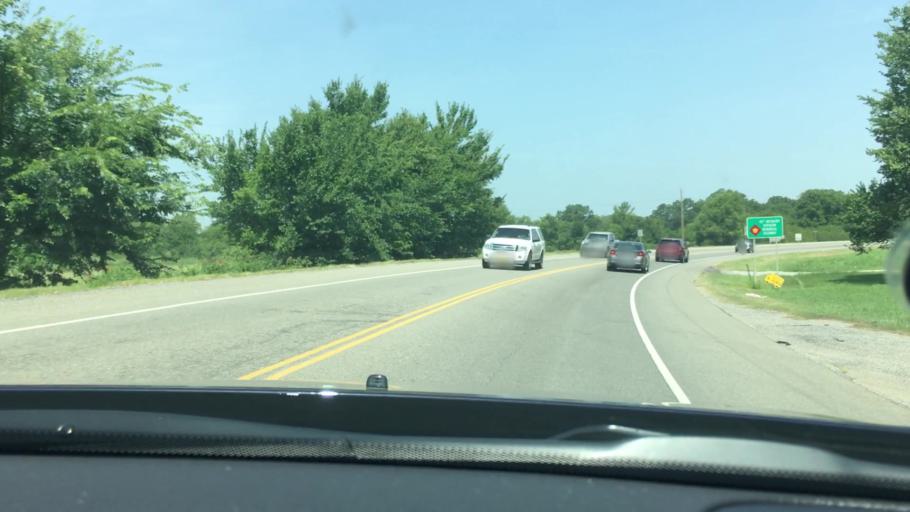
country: US
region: Oklahoma
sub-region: Coal County
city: Coalgate
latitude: 34.5420
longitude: -96.2269
